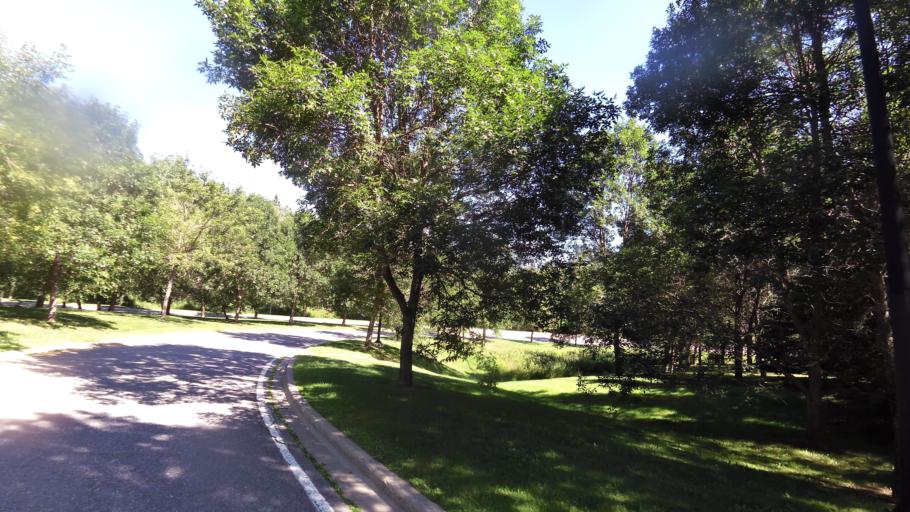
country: CA
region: Ontario
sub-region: Thunder Bay District
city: Thunder Bay
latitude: 48.4856
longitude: -89.1696
